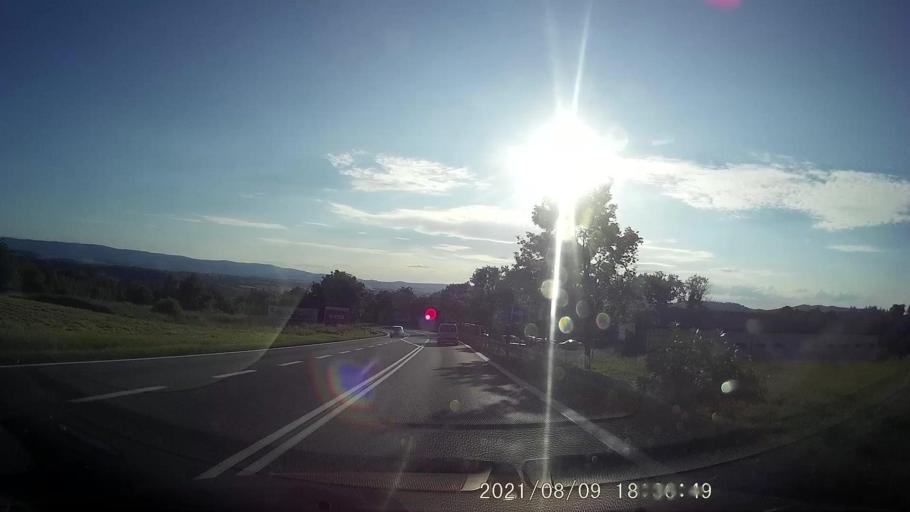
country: PL
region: Lower Silesian Voivodeship
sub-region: Powiat klodzki
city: Klodzko
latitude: 50.4643
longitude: 16.6855
